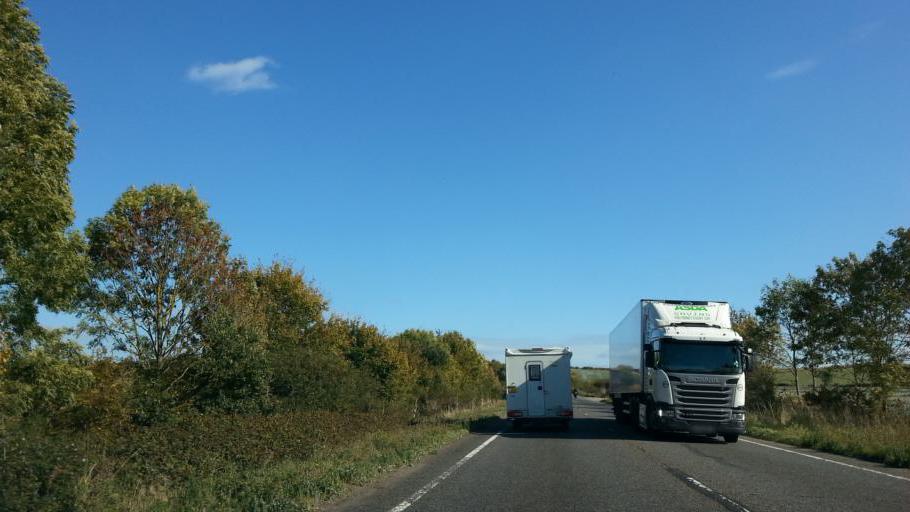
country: GB
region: England
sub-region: Peterborough
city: Castor
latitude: 52.5256
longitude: -0.3447
